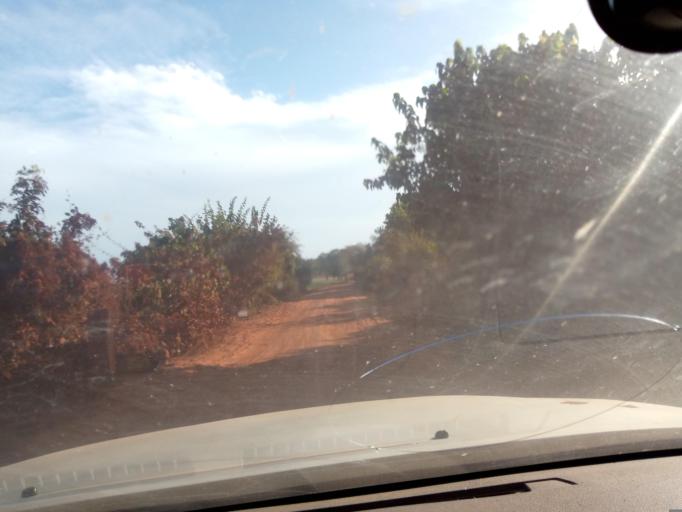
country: ML
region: Sikasso
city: Sikasso
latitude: 11.4314
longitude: -5.5571
